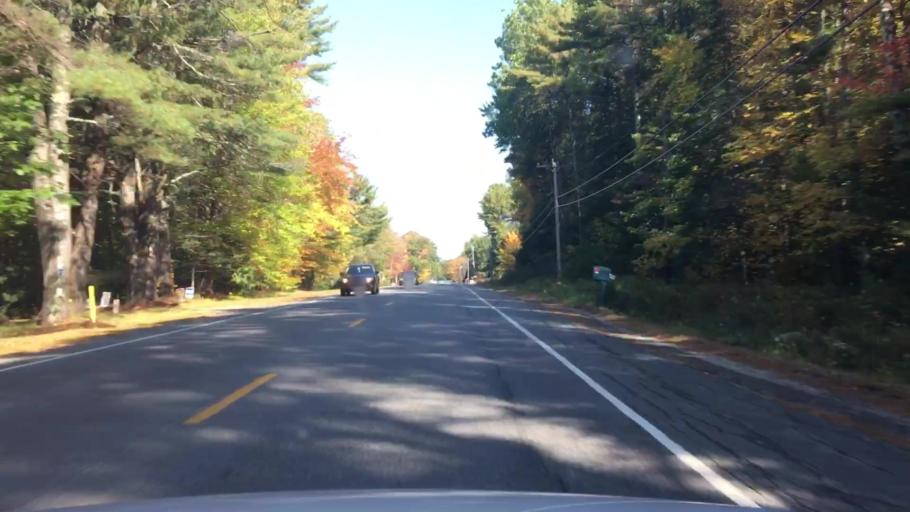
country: US
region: Maine
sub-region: Sagadahoc County
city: Topsham
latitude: 44.0154
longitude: -69.9449
